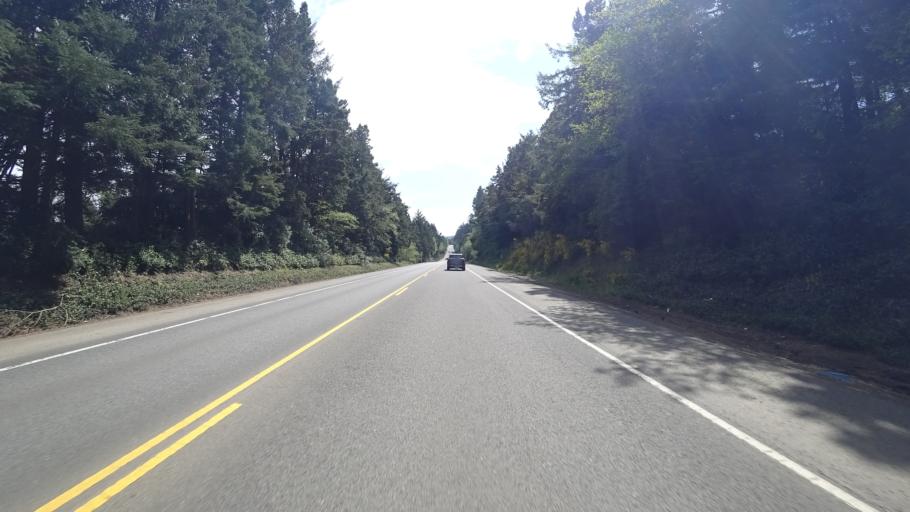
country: US
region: Oregon
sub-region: Lincoln County
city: Lincoln Beach
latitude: 44.8714
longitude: -124.0346
